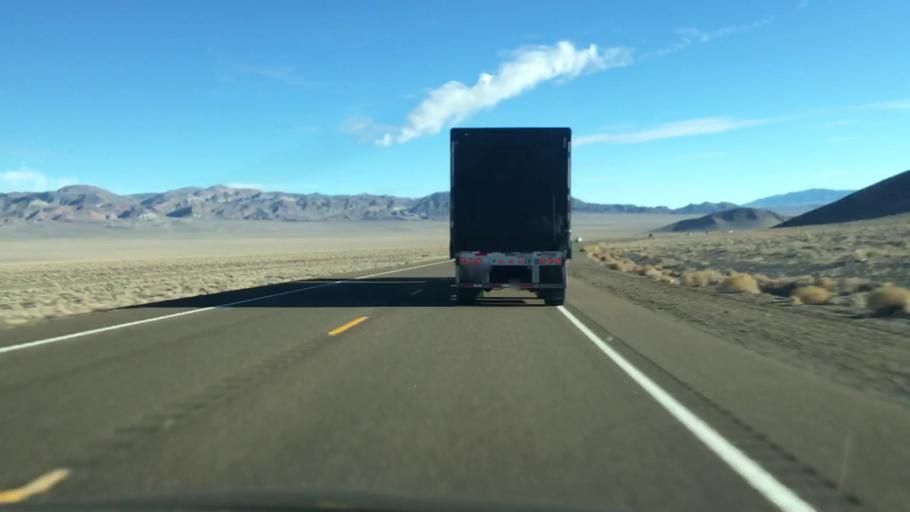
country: US
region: Nevada
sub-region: Nye County
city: Tonopah
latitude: 38.1731
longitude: -117.9592
